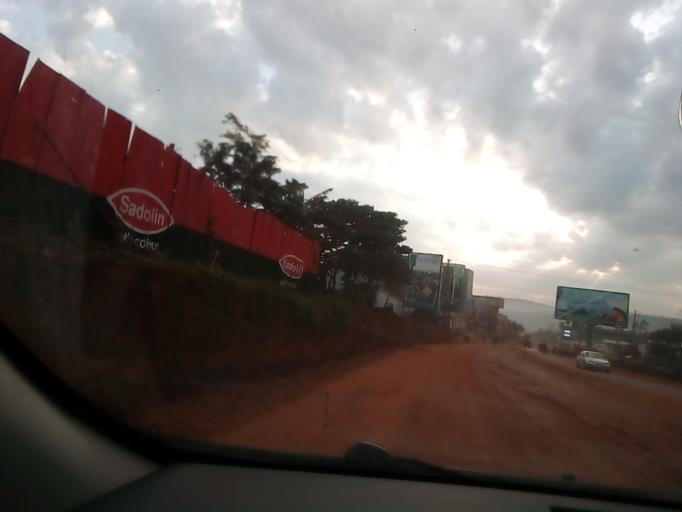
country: UG
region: Central Region
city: Masaka
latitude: -0.3341
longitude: 31.7420
